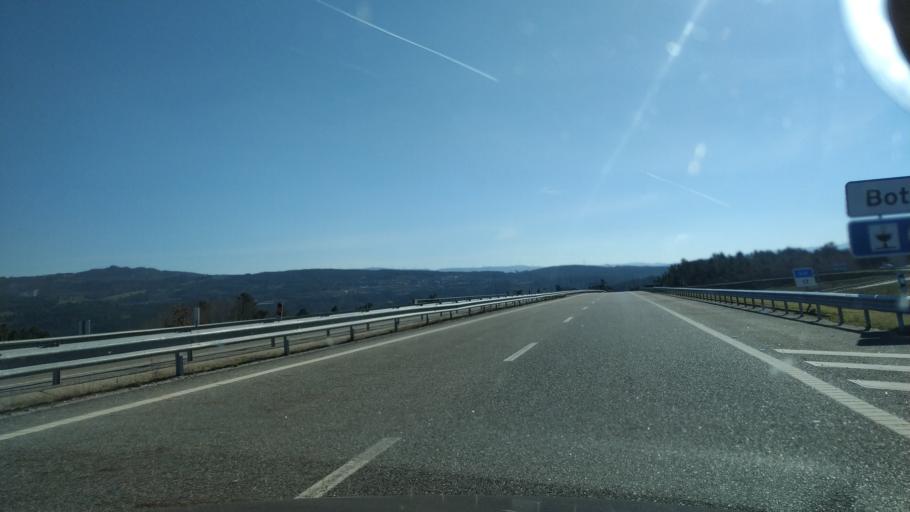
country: PT
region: Vila Real
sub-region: Chaves
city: Chaves
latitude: 41.7141
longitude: -7.5434
